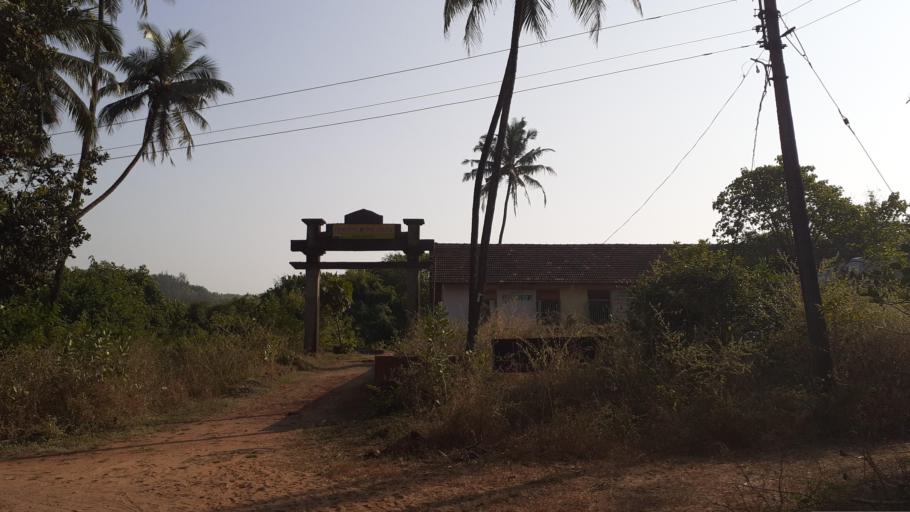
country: IN
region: Maharashtra
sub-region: Ratnagiri
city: Ratnagiri
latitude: 17.2126
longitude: 73.2479
